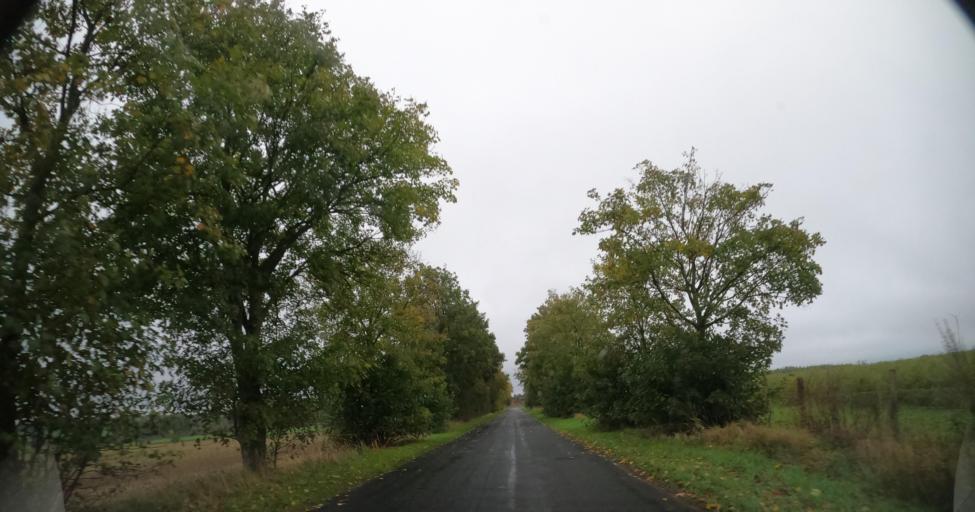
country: PL
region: West Pomeranian Voivodeship
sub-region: Powiat pyrzycki
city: Kozielice
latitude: 53.0763
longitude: 14.7839
